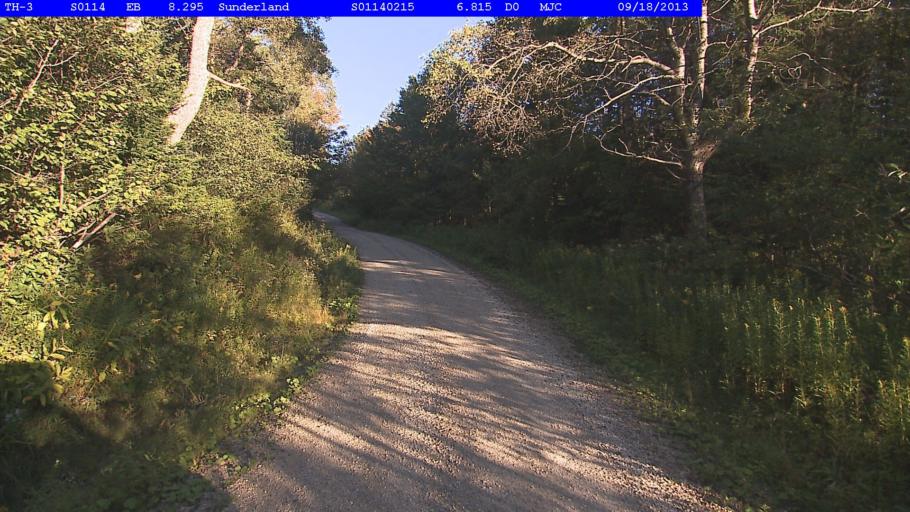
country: US
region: Vermont
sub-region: Bennington County
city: Arlington
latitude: 43.0526
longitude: -73.0528
